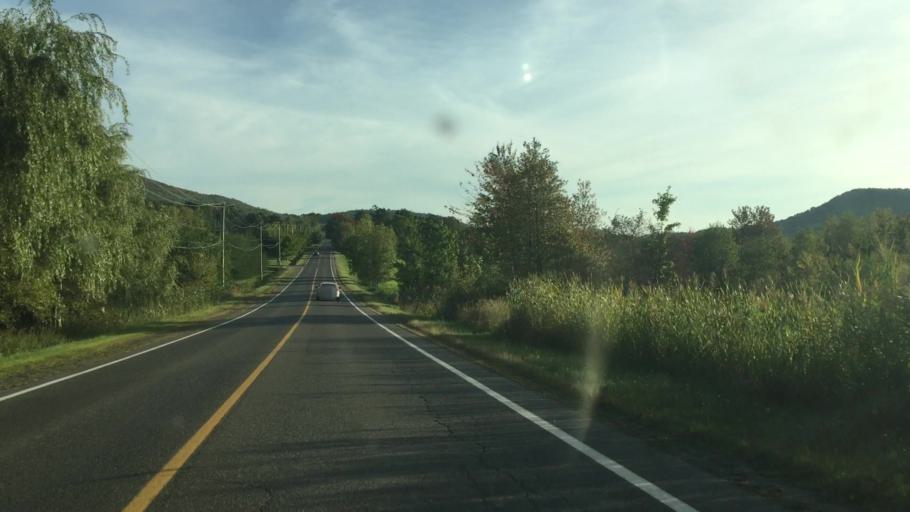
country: CA
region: Quebec
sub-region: Monteregie
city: Bromont
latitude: 45.3056
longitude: -72.6589
